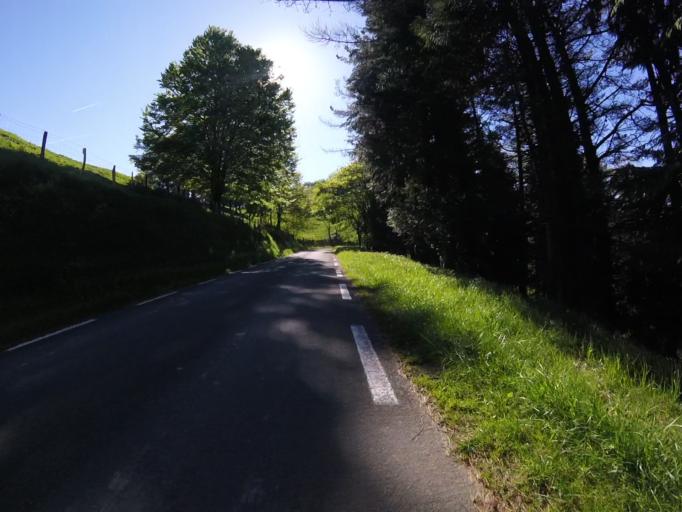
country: ES
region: Basque Country
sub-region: Provincia de Guipuzcoa
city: Aizarnazabal
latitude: 43.2163
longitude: -2.2101
